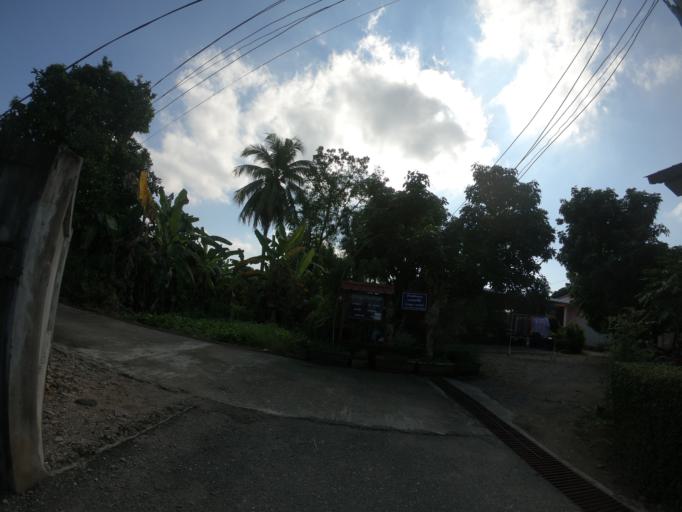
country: TH
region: Chiang Mai
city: Saraphi
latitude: 18.7065
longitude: 99.0041
